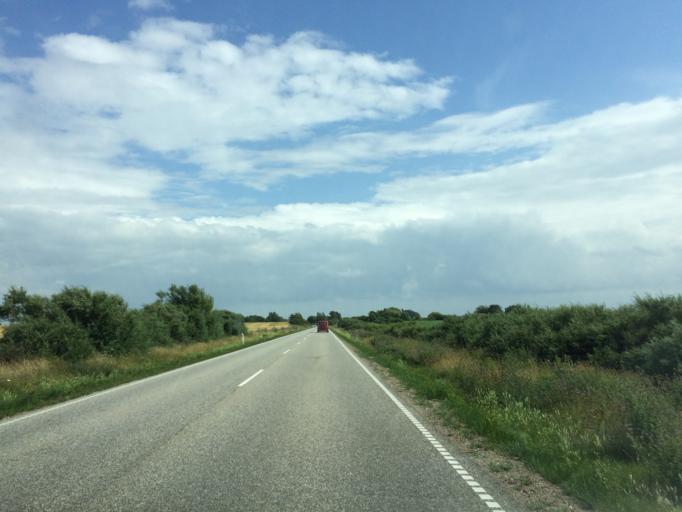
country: DK
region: Zealand
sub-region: Odsherred Kommune
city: Asnaes
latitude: 55.9683
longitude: 11.3566
